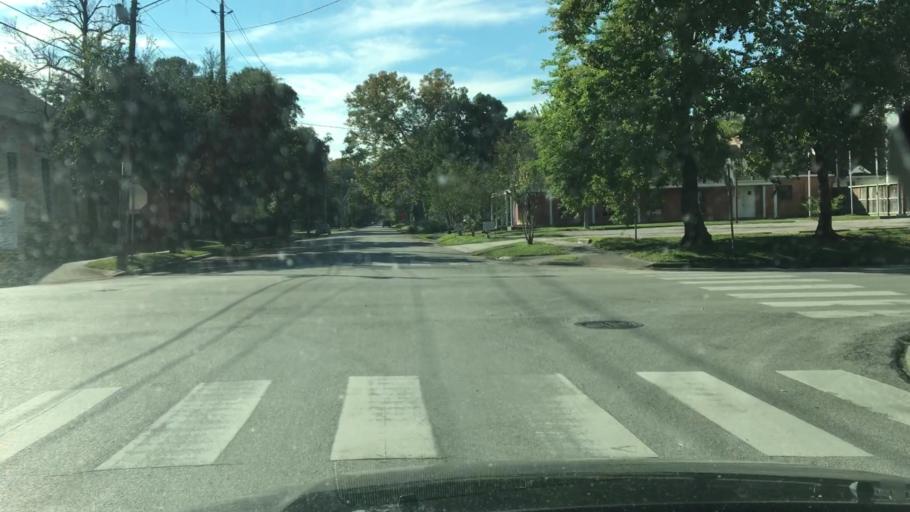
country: US
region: Texas
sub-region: Harris County
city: Houston
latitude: 29.8020
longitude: -95.4014
